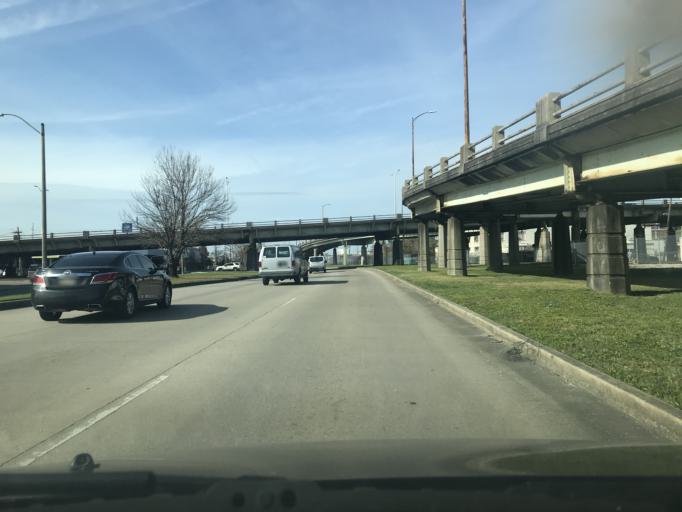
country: US
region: Louisiana
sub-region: Orleans Parish
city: New Orleans
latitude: 29.9546
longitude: -90.0953
